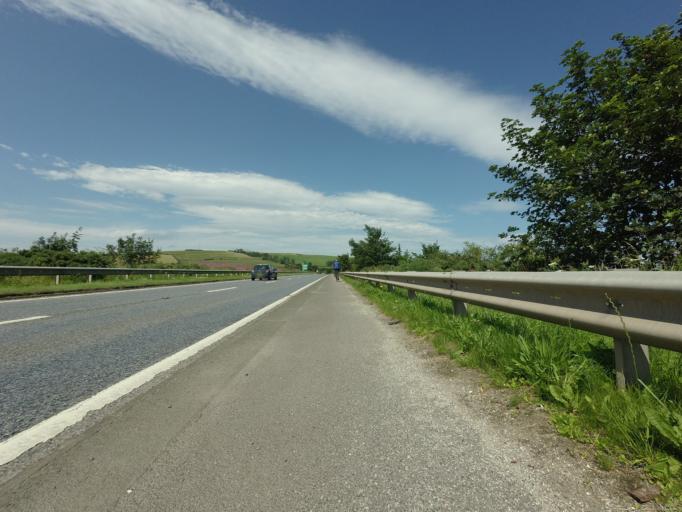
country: GB
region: Scotland
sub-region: Highland
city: Conon Bridge
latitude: 57.5751
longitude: -4.4320
